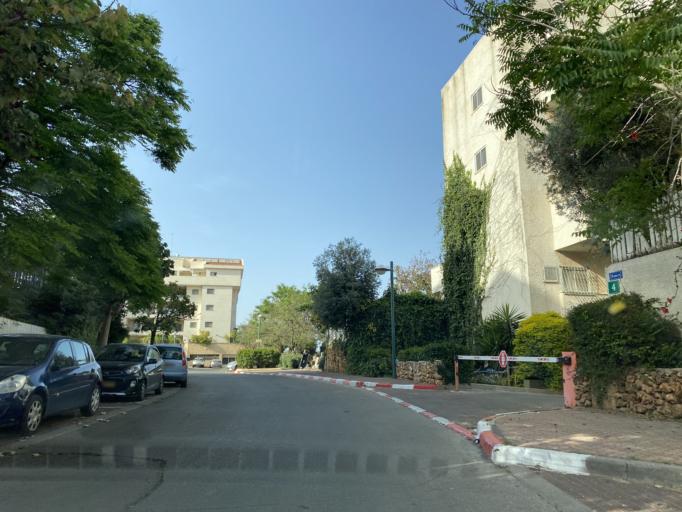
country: IL
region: Central District
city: Kfar Saba
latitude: 32.1831
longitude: 34.9151
